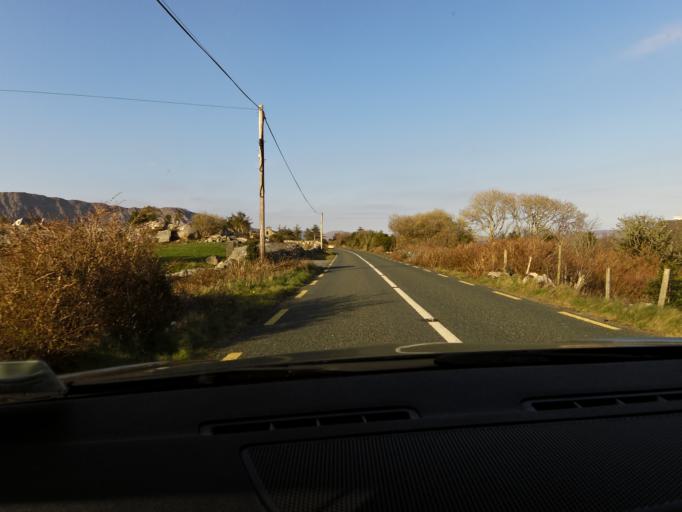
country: IE
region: Connaught
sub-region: County Galway
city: Clifden
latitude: 53.3497
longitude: -9.7080
